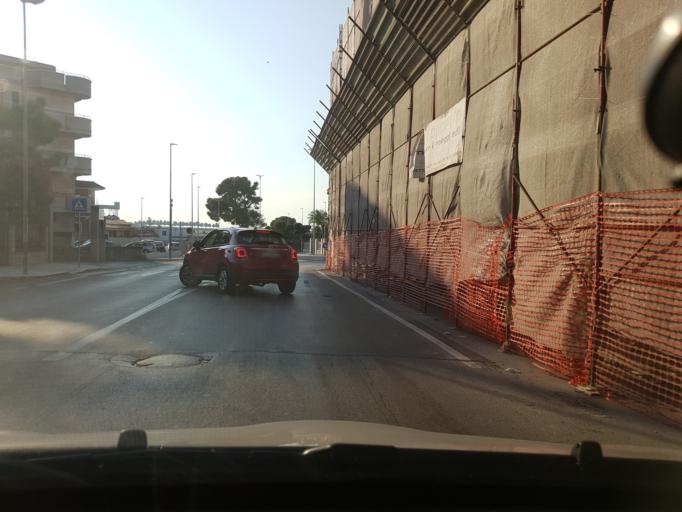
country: IT
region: Apulia
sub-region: Provincia di Foggia
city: Cerignola
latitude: 41.2667
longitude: 15.8861
